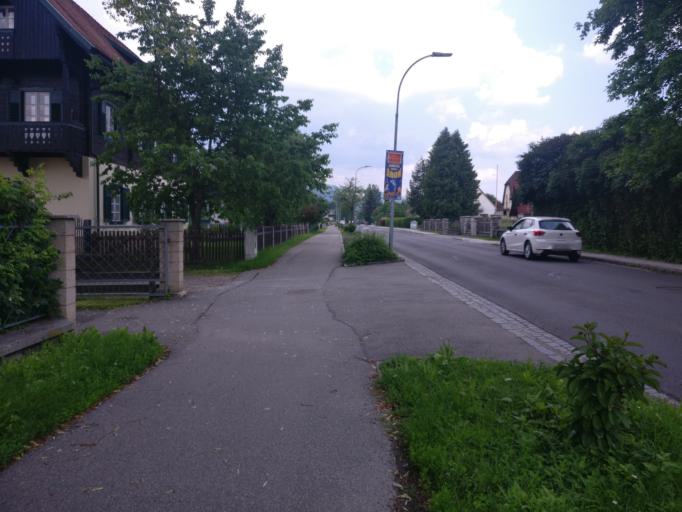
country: AT
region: Styria
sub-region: Politischer Bezirk Bruck-Muerzzuschlag
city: Krieglach
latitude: 47.5491
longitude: 15.5658
